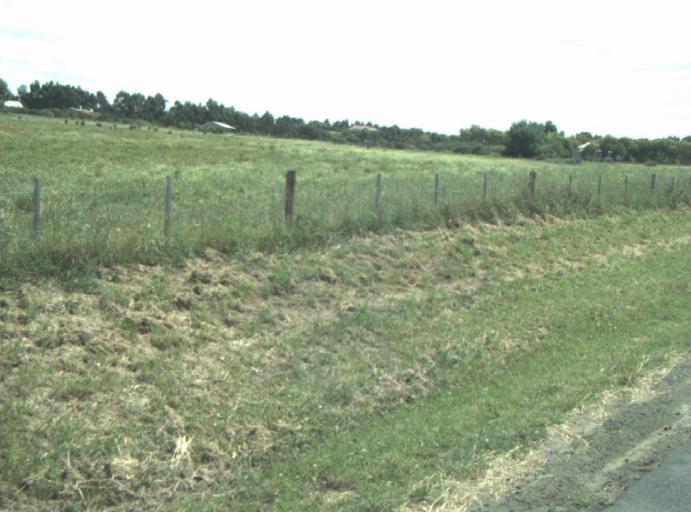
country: AU
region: Victoria
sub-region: Greater Geelong
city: Clifton Springs
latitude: -38.1569
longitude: 144.5868
